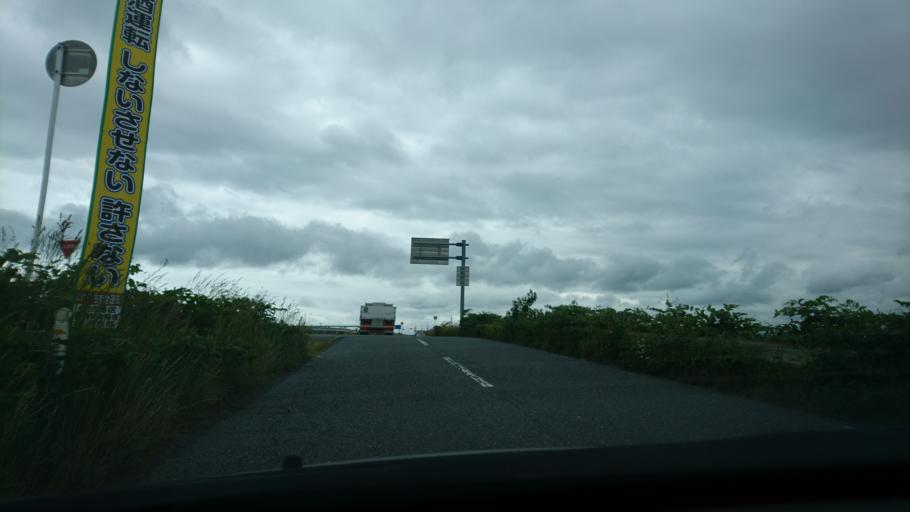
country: JP
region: Miyagi
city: Wakuya
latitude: 38.7264
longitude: 141.2629
